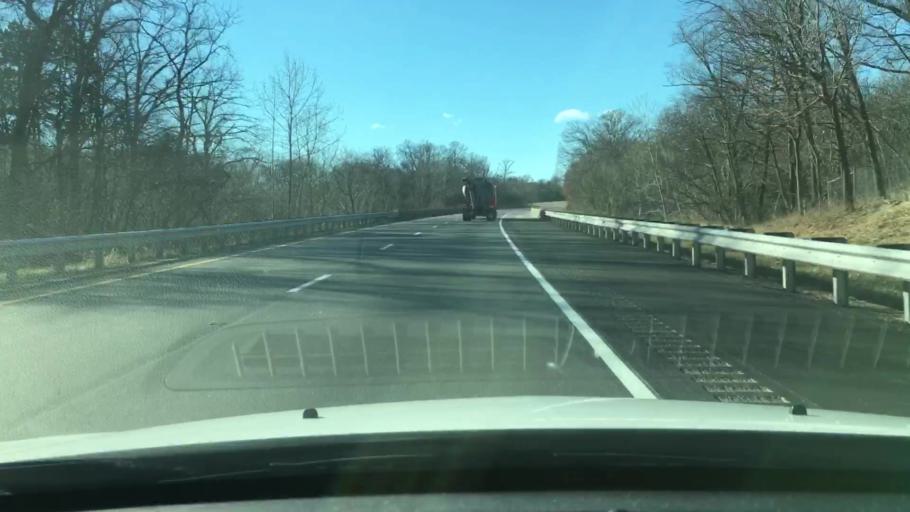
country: US
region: Illinois
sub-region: Pike County
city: Griggsville
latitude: 39.6825
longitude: -90.6569
